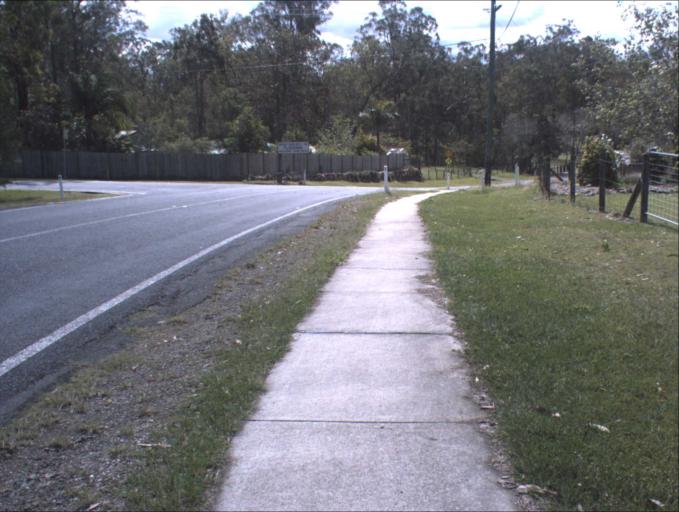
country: AU
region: Queensland
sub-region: Logan
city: North Maclean
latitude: -27.7479
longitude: 153.0147
